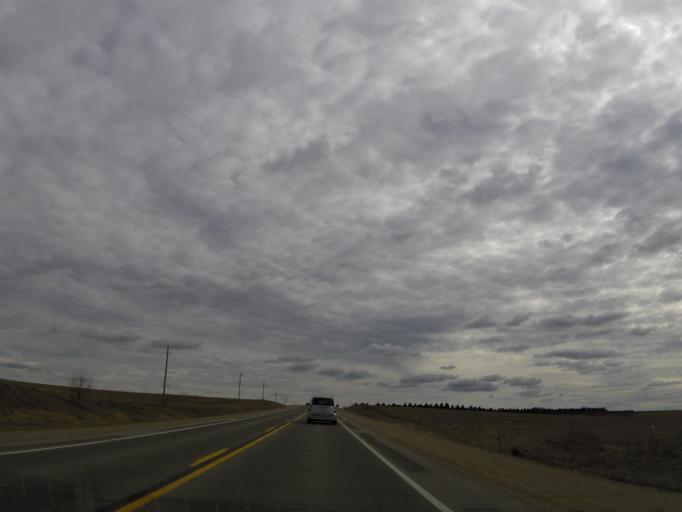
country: US
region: Iowa
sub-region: Chickasaw County
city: New Hampton
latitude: 43.1957
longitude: -92.2982
